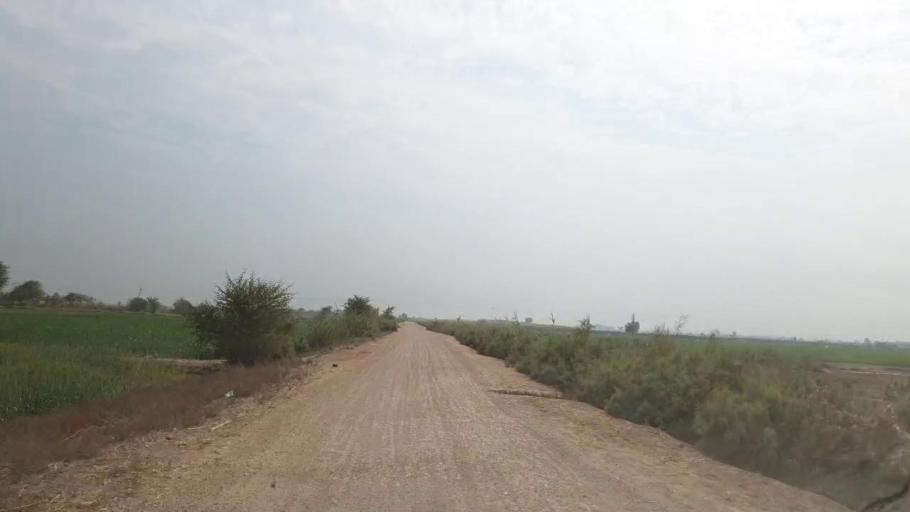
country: PK
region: Sindh
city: Mirpur Khas
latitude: 25.5433
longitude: 69.1267
